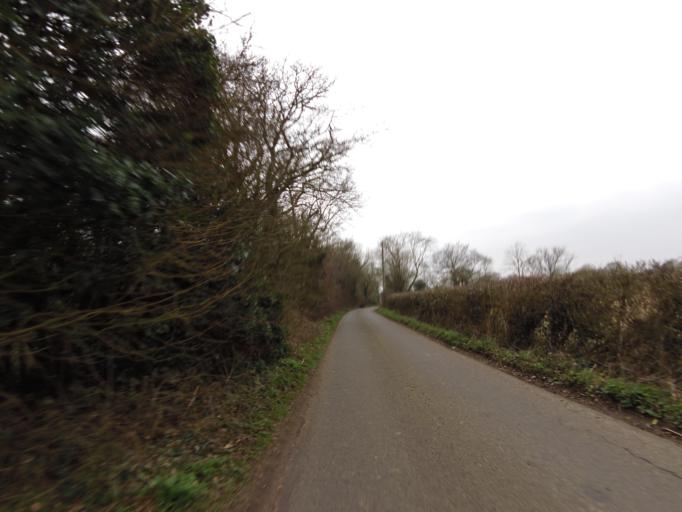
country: GB
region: England
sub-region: Suffolk
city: Framlingham
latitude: 52.2317
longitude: 1.3542
